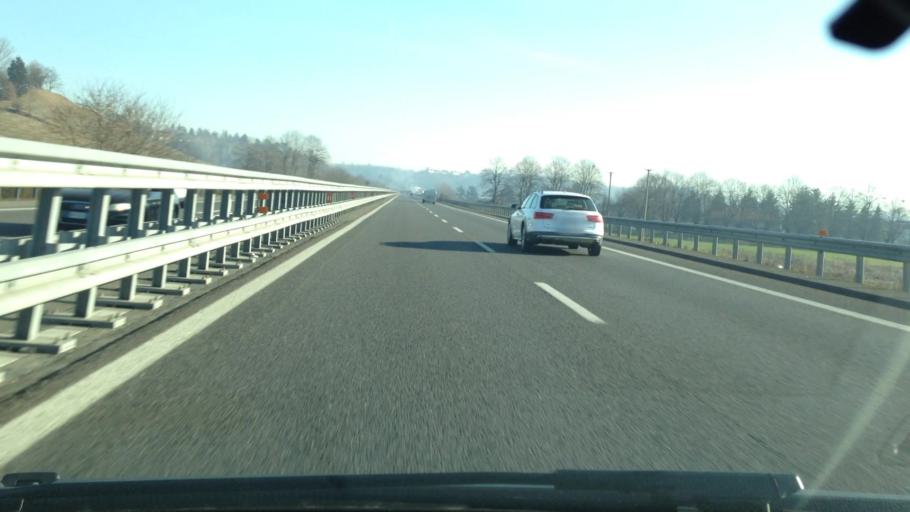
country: IT
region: Piedmont
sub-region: Provincia di Asti
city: Azzano d'Asti
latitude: 44.9096
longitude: 8.2621
